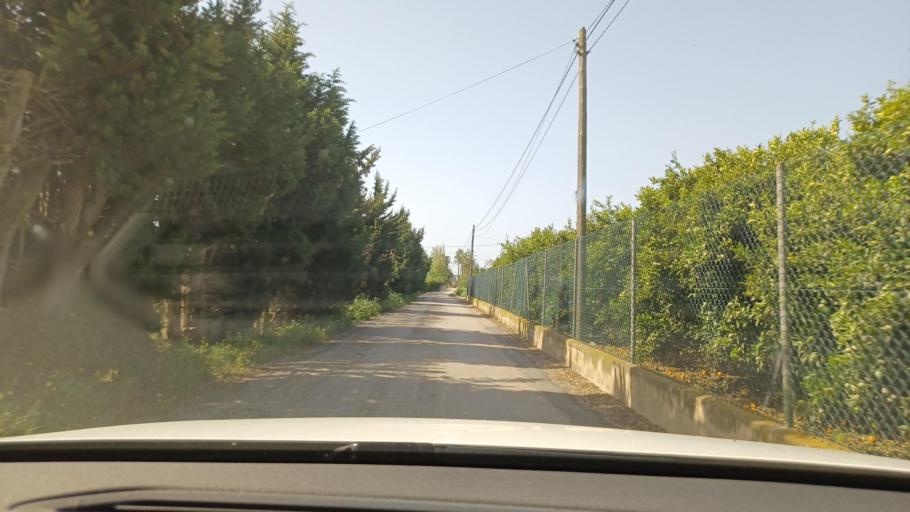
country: ES
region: Catalonia
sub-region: Provincia de Tarragona
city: Tortosa
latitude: 40.7950
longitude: 0.5158
